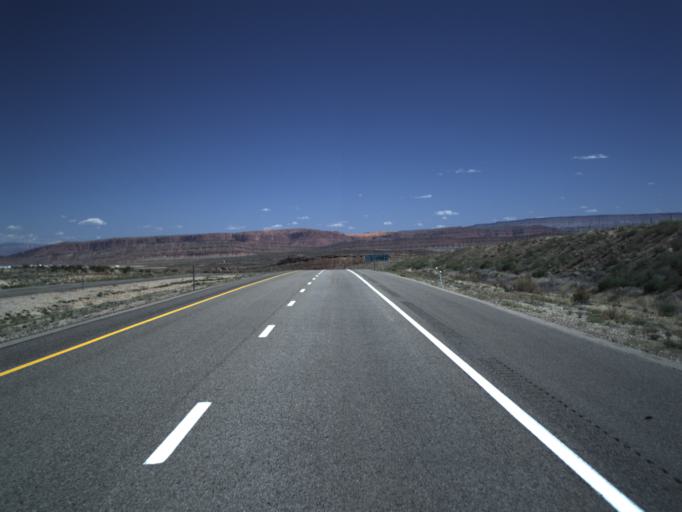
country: US
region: Utah
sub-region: Washington County
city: Saint George
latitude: 37.0030
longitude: -113.5453
